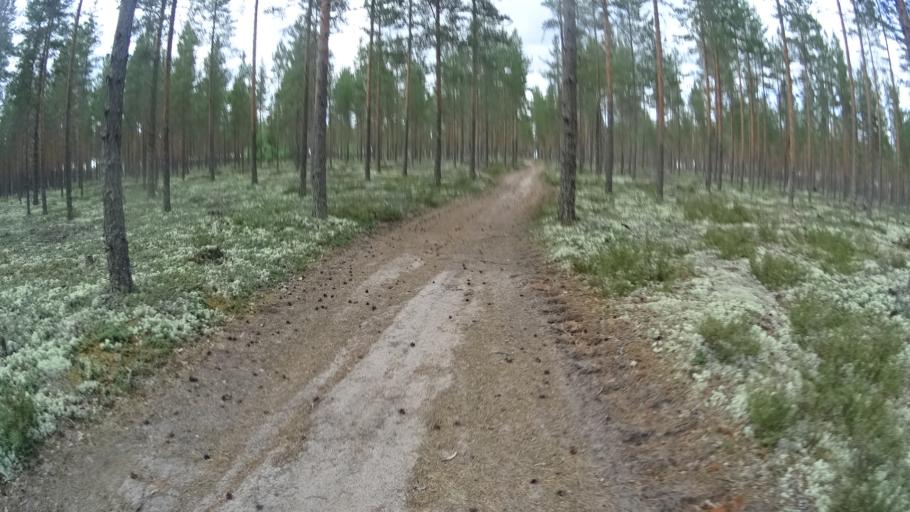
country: FI
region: Satakunta
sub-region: Pohjois-Satakunta
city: Jaemijaervi
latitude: 61.7680
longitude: 22.8024
